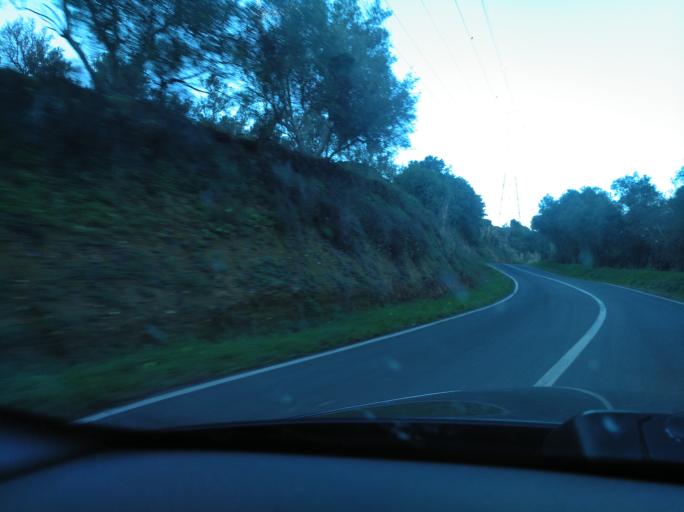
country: PT
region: Lisbon
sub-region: Loures
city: Unhos
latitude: 38.8143
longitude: -9.1136
